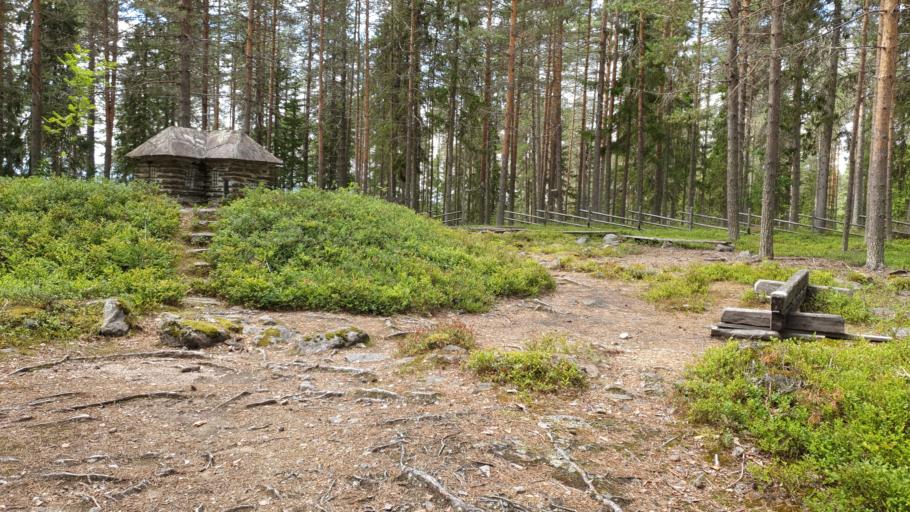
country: FI
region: Kainuu
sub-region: Kehys-Kainuu
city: Kuhmo
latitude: 64.3815
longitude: 29.8072
